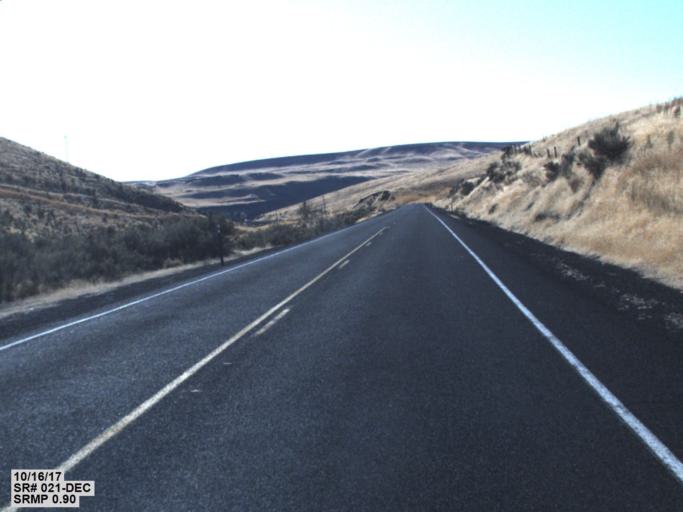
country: US
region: Washington
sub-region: Franklin County
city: Connell
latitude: 46.6544
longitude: -118.5505
